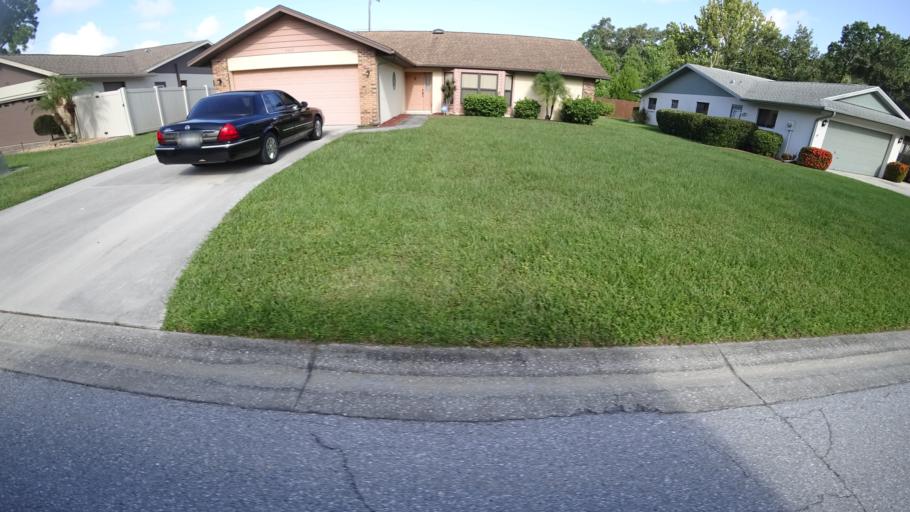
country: US
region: Florida
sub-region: Sarasota County
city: Desoto Lakes
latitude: 27.3901
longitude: -82.5011
